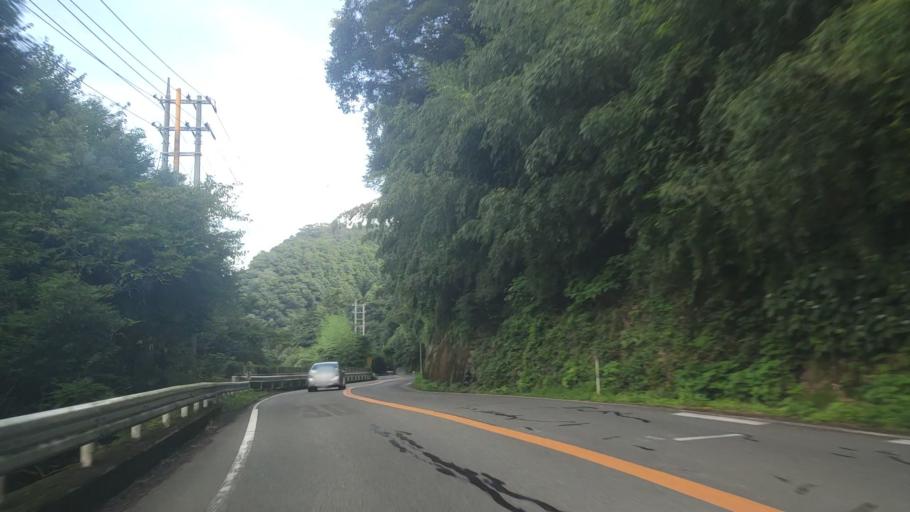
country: JP
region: Gunma
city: Omamacho-omama
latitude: 36.4561
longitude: 139.2651
